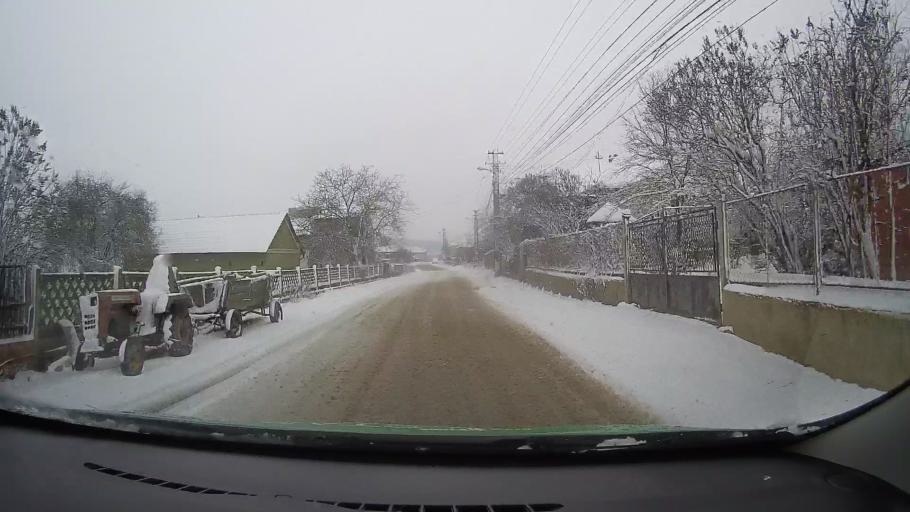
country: RO
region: Hunedoara
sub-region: Municipiul Hunedoara
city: Pestisu Mare
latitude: 45.7966
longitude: 22.9115
